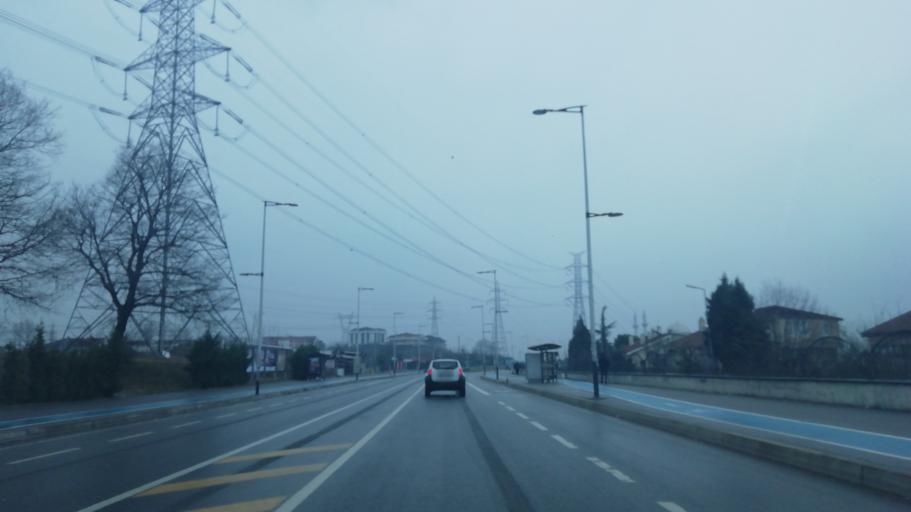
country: TR
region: Sakarya
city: Kazimpasa
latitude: 40.7451
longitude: 30.3429
